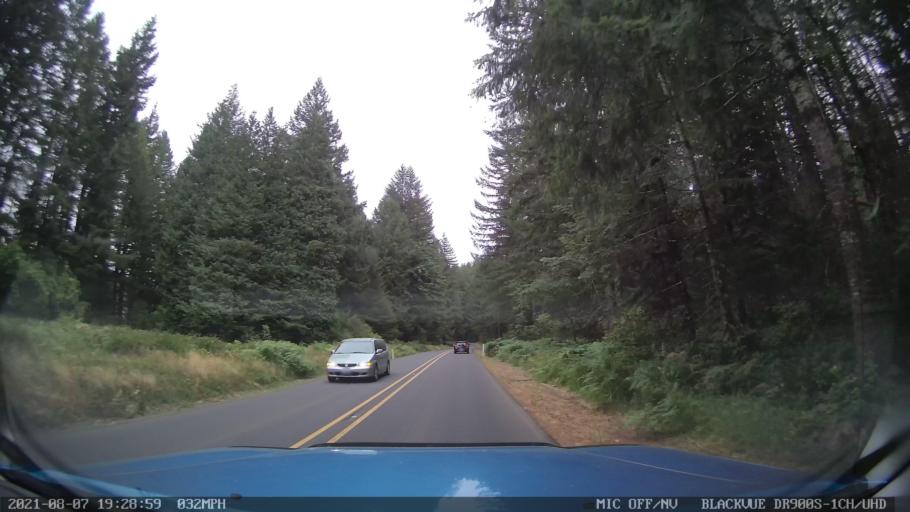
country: US
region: Oregon
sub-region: Linn County
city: Lyons
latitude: 44.8841
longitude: -122.6347
